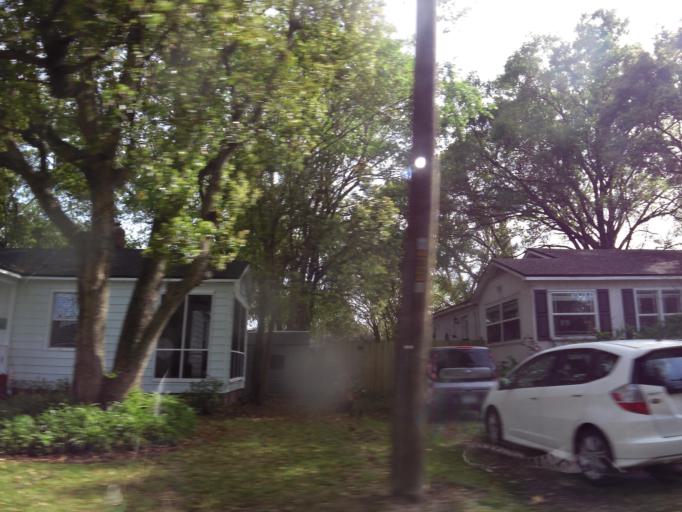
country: US
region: Florida
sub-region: Duval County
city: Jacksonville
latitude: 30.3160
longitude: -81.7274
